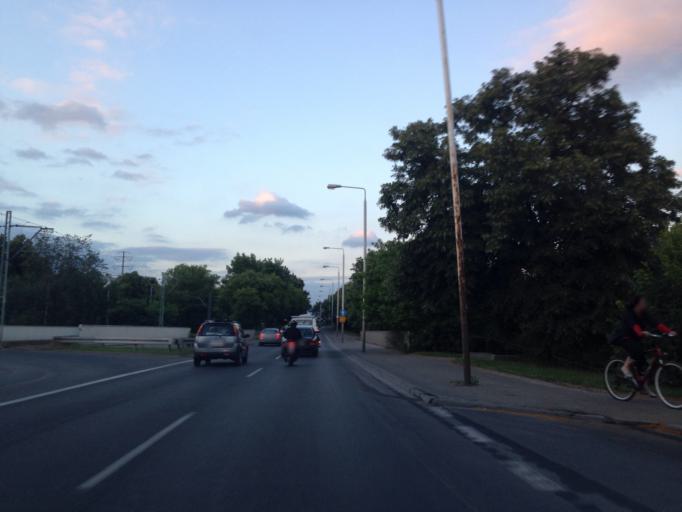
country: PL
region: Masovian Voivodeship
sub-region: Warszawa
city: Zoliborz
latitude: 52.2587
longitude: 21.0033
